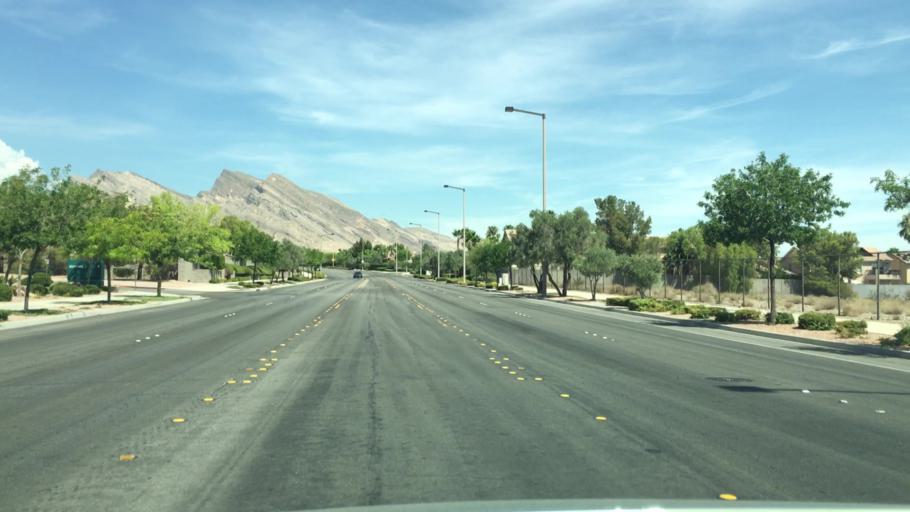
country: US
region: Nevada
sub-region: Clark County
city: Summerlin South
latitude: 36.1831
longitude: -115.3161
